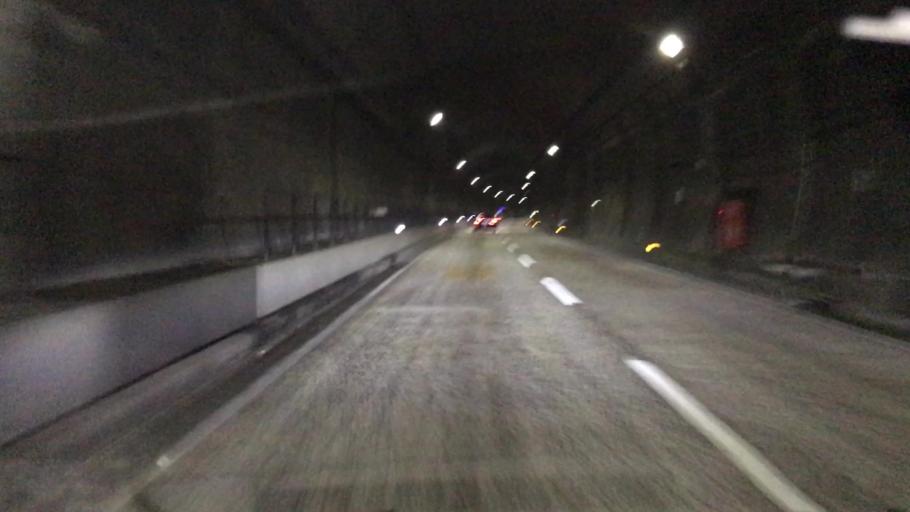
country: JP
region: Hyogo
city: Kobe
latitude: 34.7417
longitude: 135.1717
